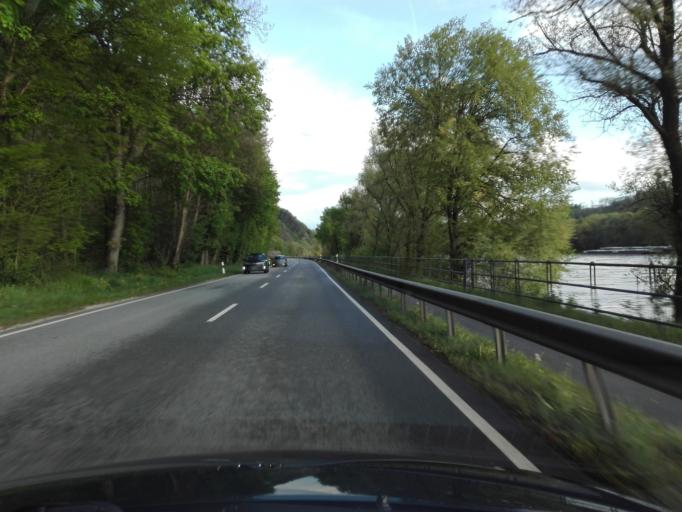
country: DE
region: Bavaria
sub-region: Lower Bavaria
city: Thyrnau
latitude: 48.5837
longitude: 13.5346
